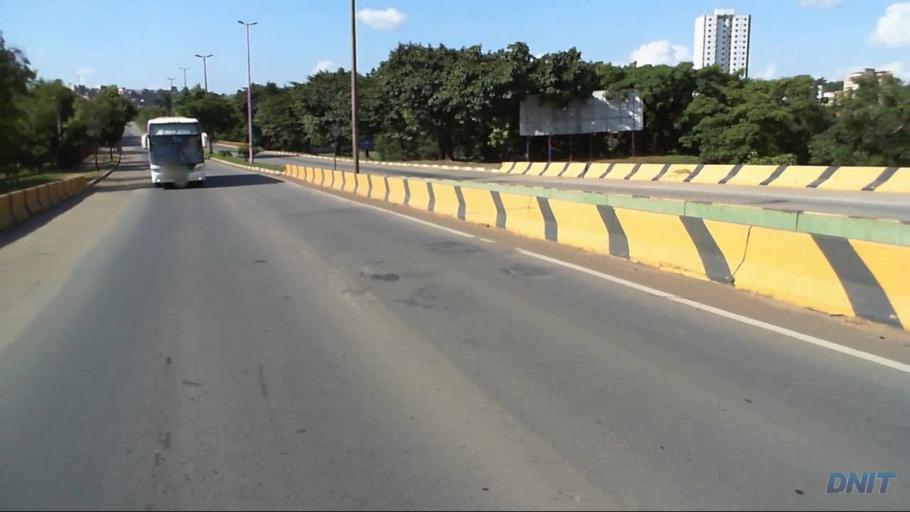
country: BR
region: Minas Gerais
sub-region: Ipatinga
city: Ipatinga
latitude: -19.4697
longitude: -42.5383
